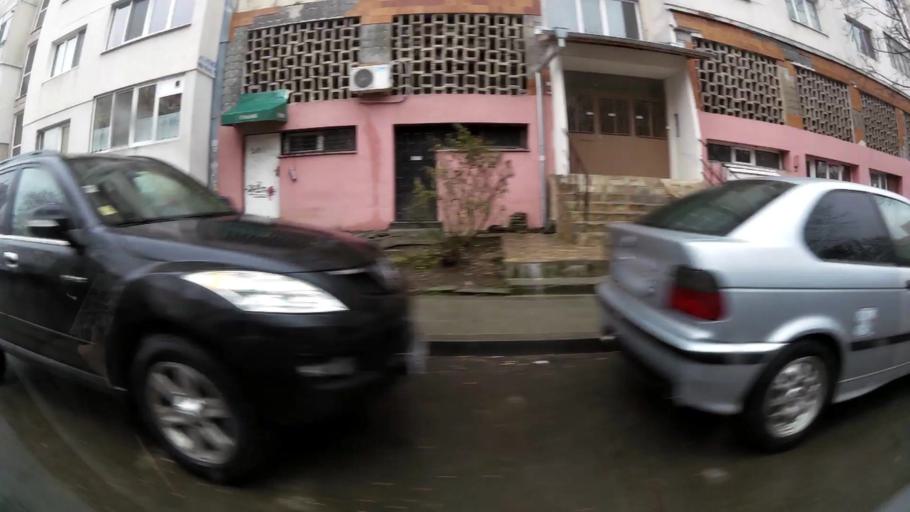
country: BG
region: Sofia-Capital
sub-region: Stolichna Obshtina
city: Sofia
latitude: 42.6412
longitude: 23.3745
